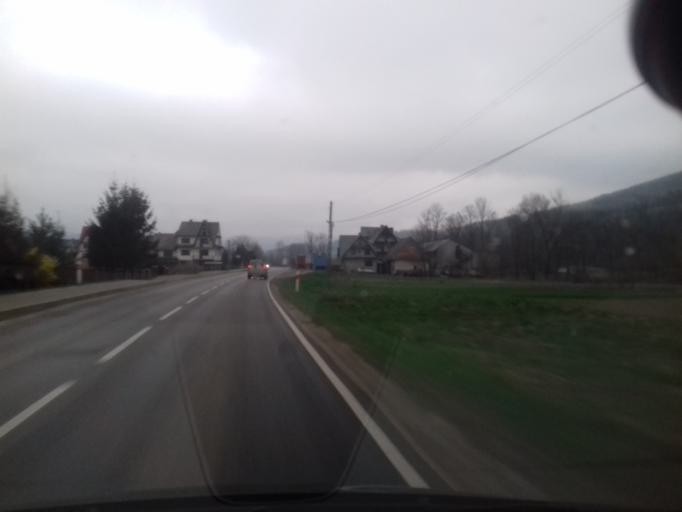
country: PL
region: Lesser Poland Voivodeship
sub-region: Powiat myslenicki
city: Lubien
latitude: 49.7081
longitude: 20.0207
